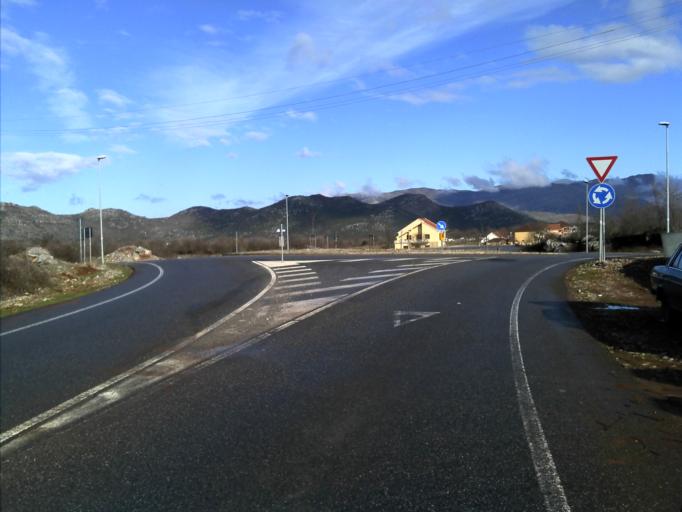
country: AL
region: Shkoder
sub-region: Rrethi i Malesia e Madhe
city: Koplik
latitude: 42.2872
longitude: 19.4400
